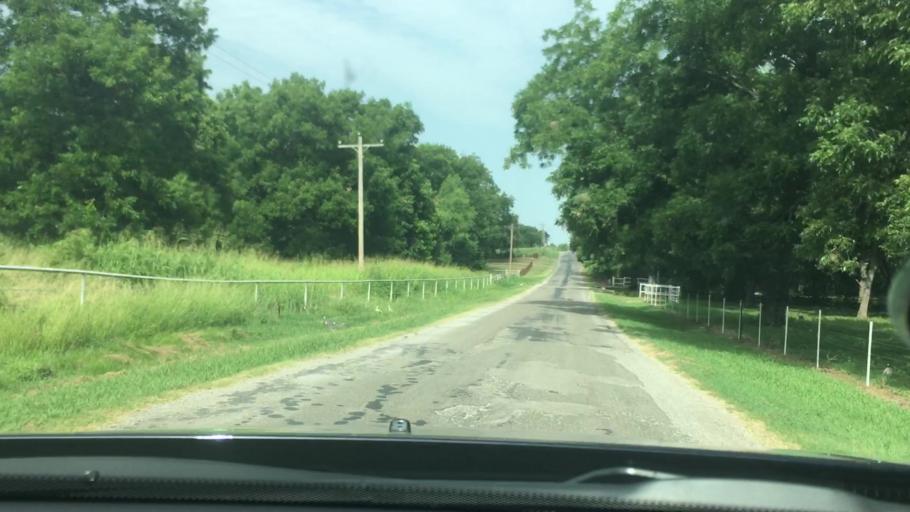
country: US
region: Oklahoma
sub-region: Garvin County
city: Pauls Valley
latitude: 34.7968
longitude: -97.1897
